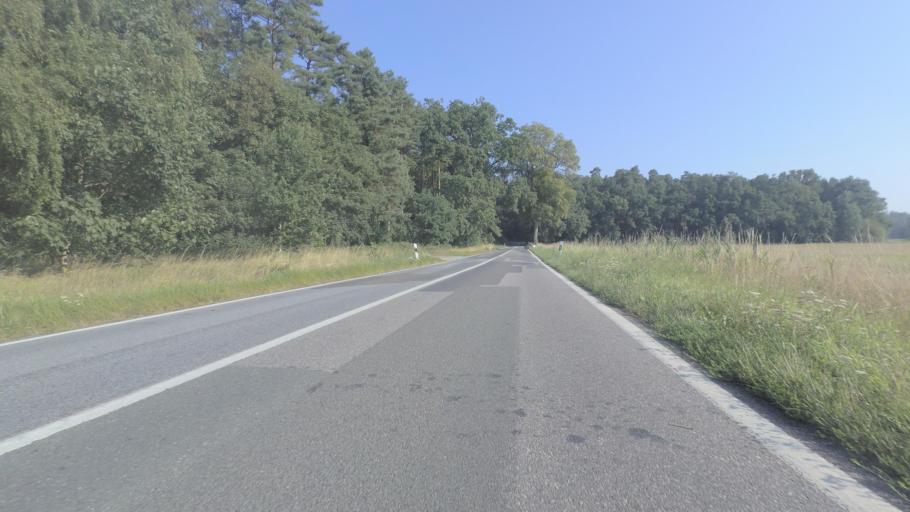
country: DE
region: Mecklenburg-Vorpommern
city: Malchow
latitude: 53.4504
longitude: 12.4310
